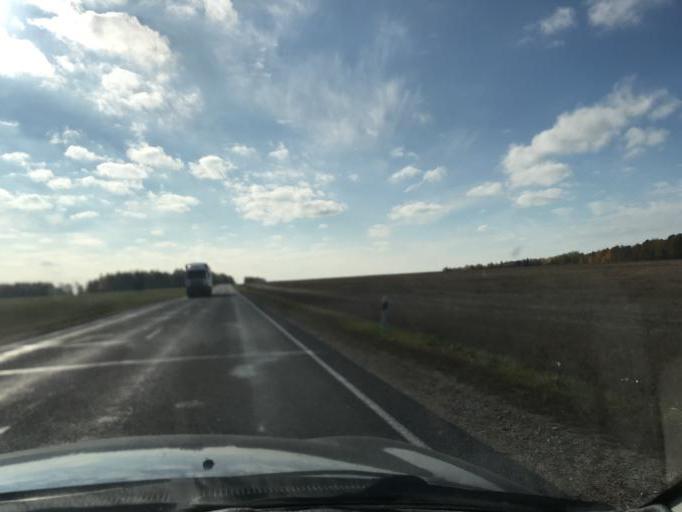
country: BY
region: Grodnenskaya
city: Voranava
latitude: 54.1963
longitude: 25.3463
